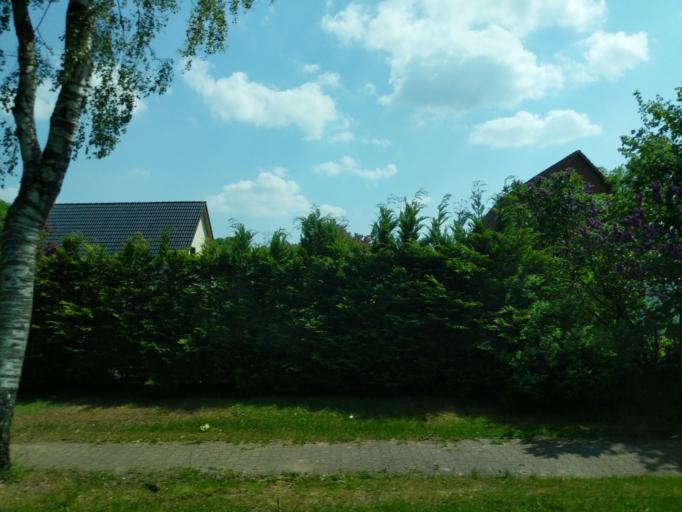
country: DE
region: Mecklenburg-Vorpommern
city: Stralendorf
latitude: 53.4959
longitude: 11.2854
